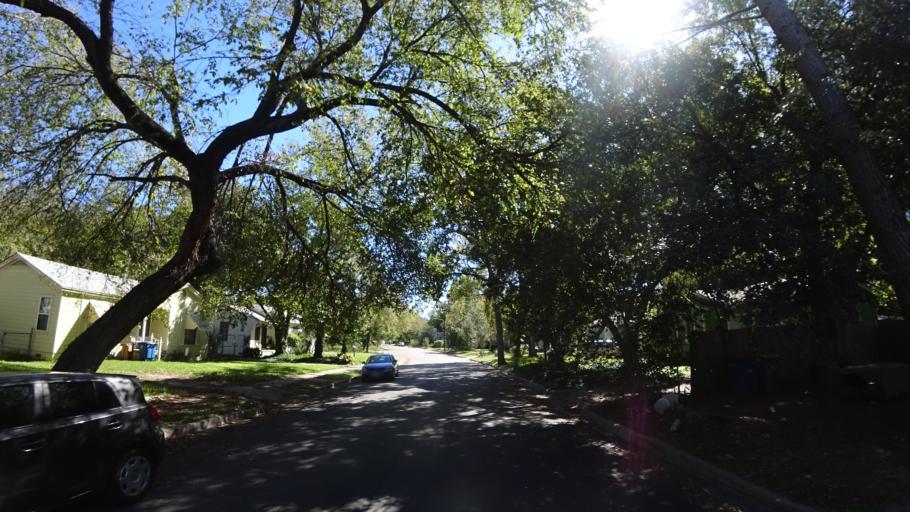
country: US
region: Texas
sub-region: Travis County
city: Austin
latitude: 30.2855
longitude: -97.7077
